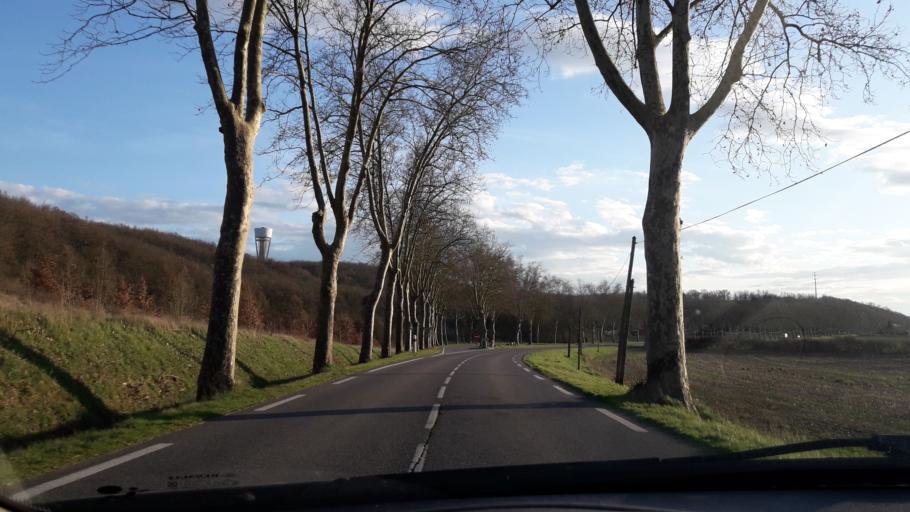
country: FR
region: Midi-Pyrenees
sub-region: Departement de la Haute-Garonne
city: Grenade
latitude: 43.7434
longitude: 1.2649
